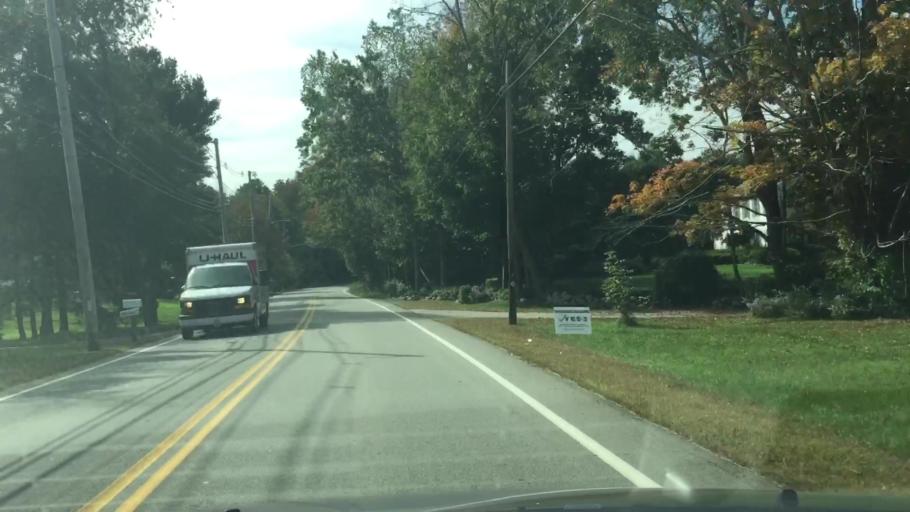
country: US
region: Massachusetts
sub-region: Essex County
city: Methuen
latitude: 42.6799
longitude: -71.2185
